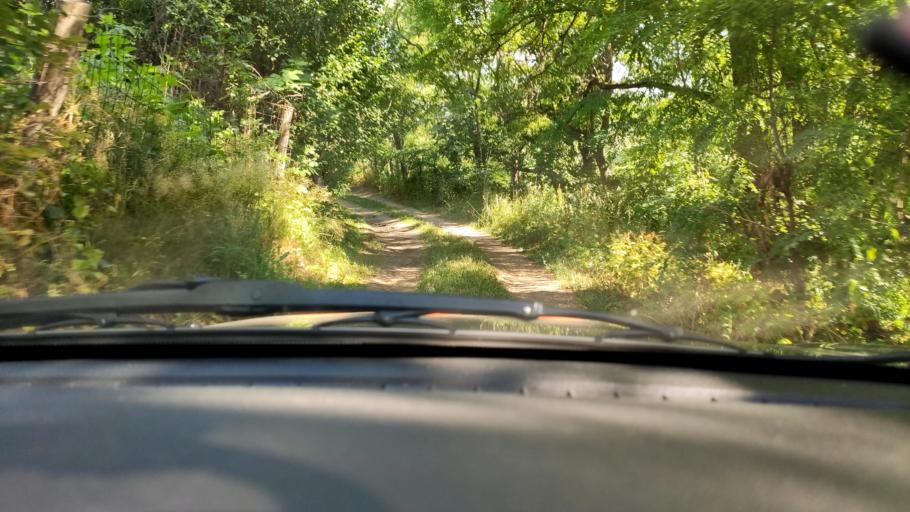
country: RU
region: Voronezj
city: Ramon'
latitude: 51.8224
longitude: 39.2703
